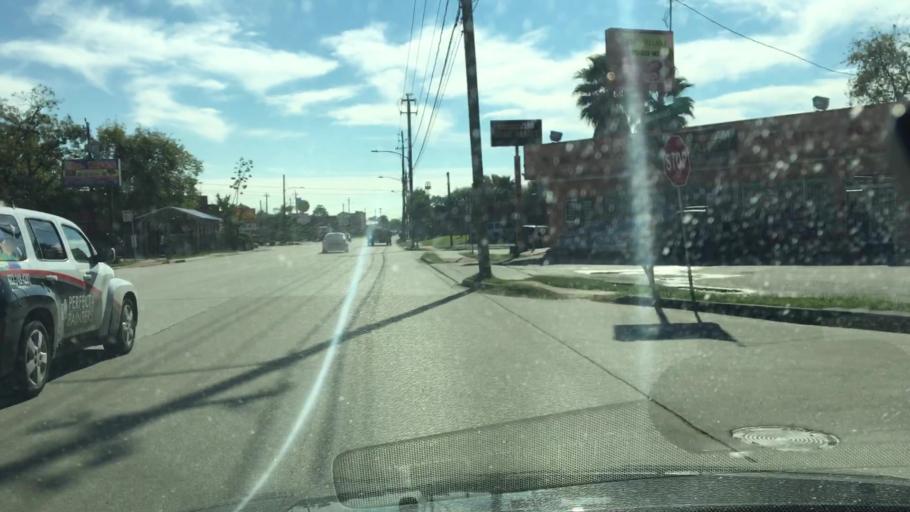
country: US
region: Texas
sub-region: Harris County
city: Houston
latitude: 29.7941
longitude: -95.3775
